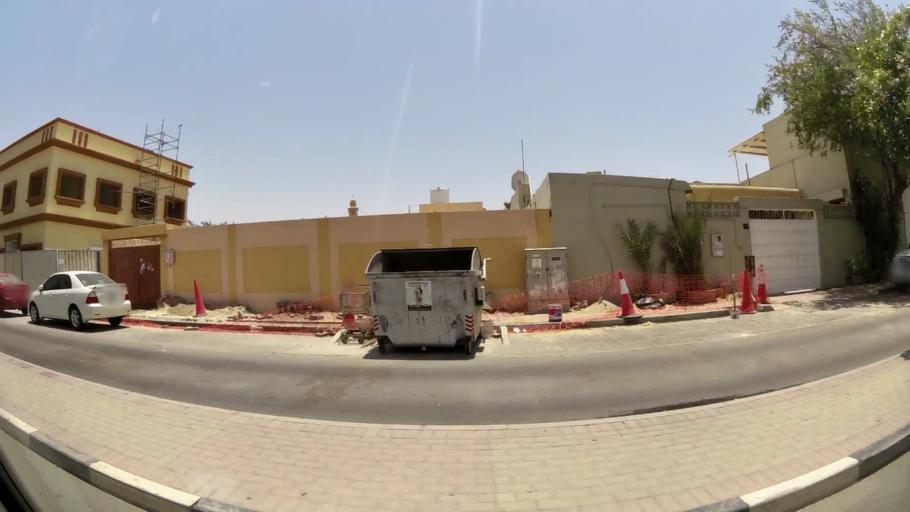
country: AE
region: Ash Shariqah
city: Sharjah
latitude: 25.2860
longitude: 55.3357
